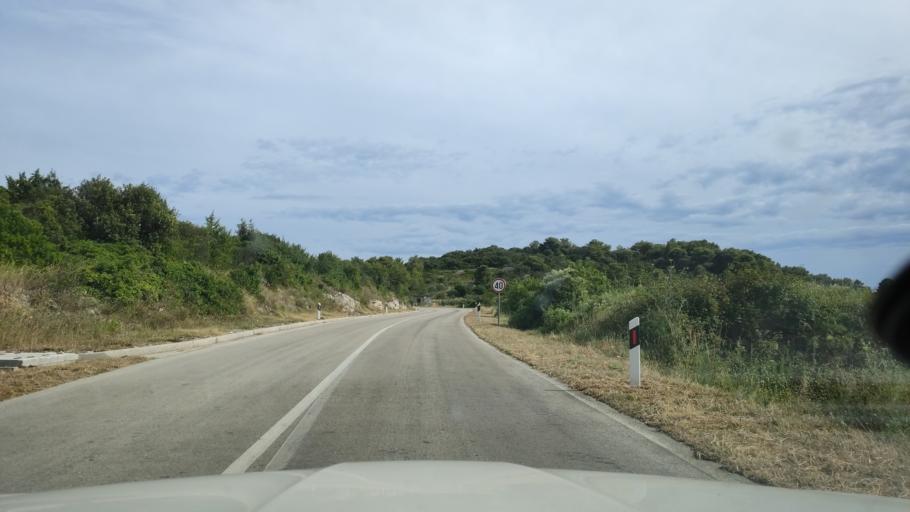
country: HR
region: Splitsko-Dalmatinska
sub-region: Grad Vis
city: Vis
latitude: 43.0389
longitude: 16.2007
